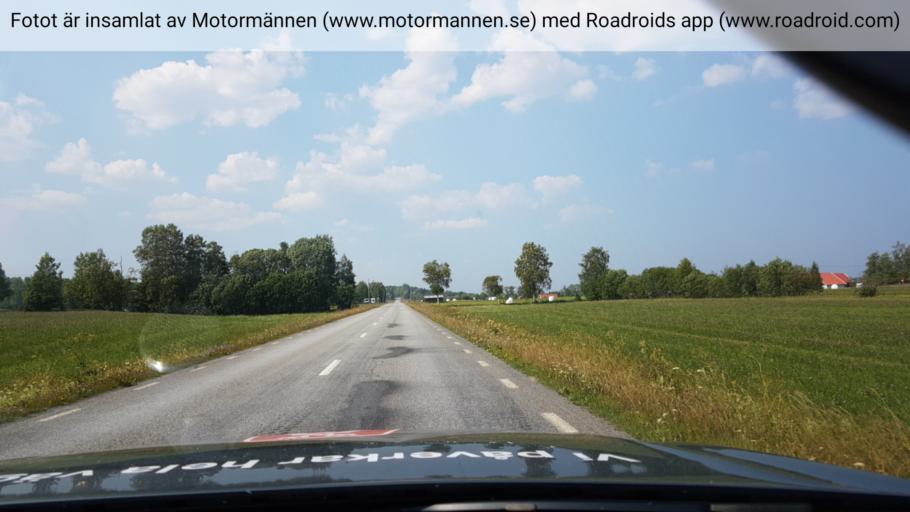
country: SE
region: Jaemtland
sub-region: Krokoms Kommun
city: Krokom
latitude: 63.1437
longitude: 14.1794
